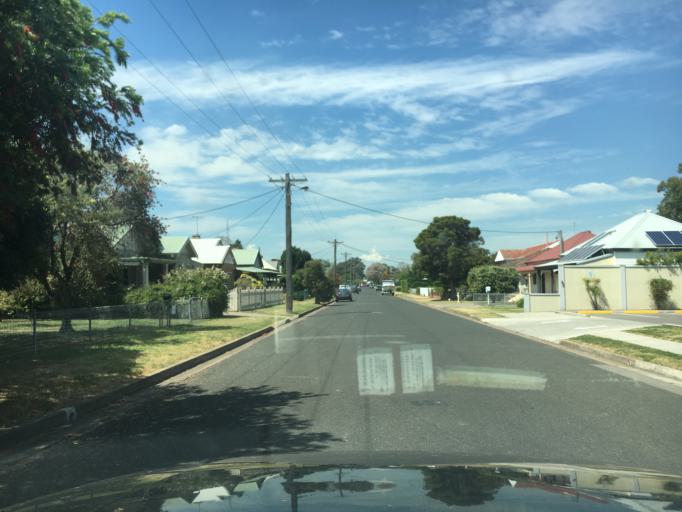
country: AU
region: New South Wales
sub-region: Singleton
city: Singleton
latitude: -32.5665
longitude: 151.1730
